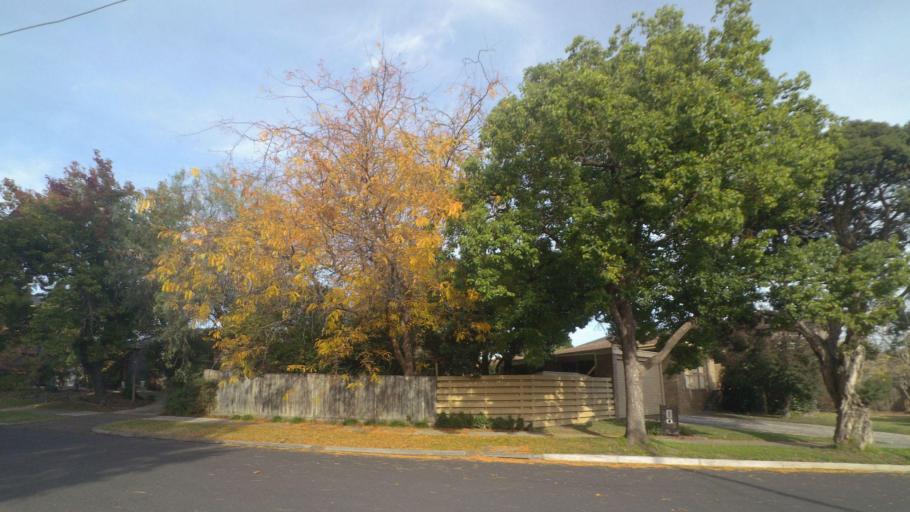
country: AU
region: Victoria
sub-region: Manningham
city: Doncaster East
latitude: -37.7777
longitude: 145.1570
